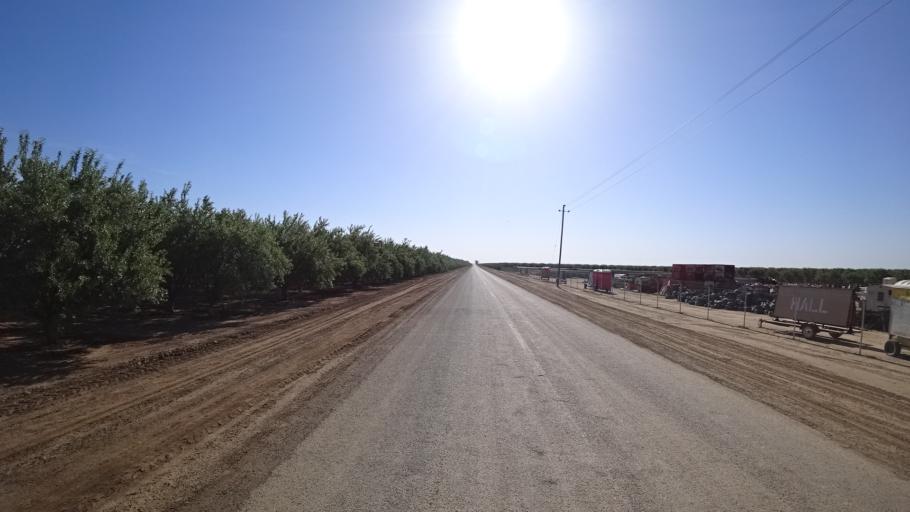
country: US
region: California
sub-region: Fresno County
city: Huron
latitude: 36.1088
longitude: -120.0385
